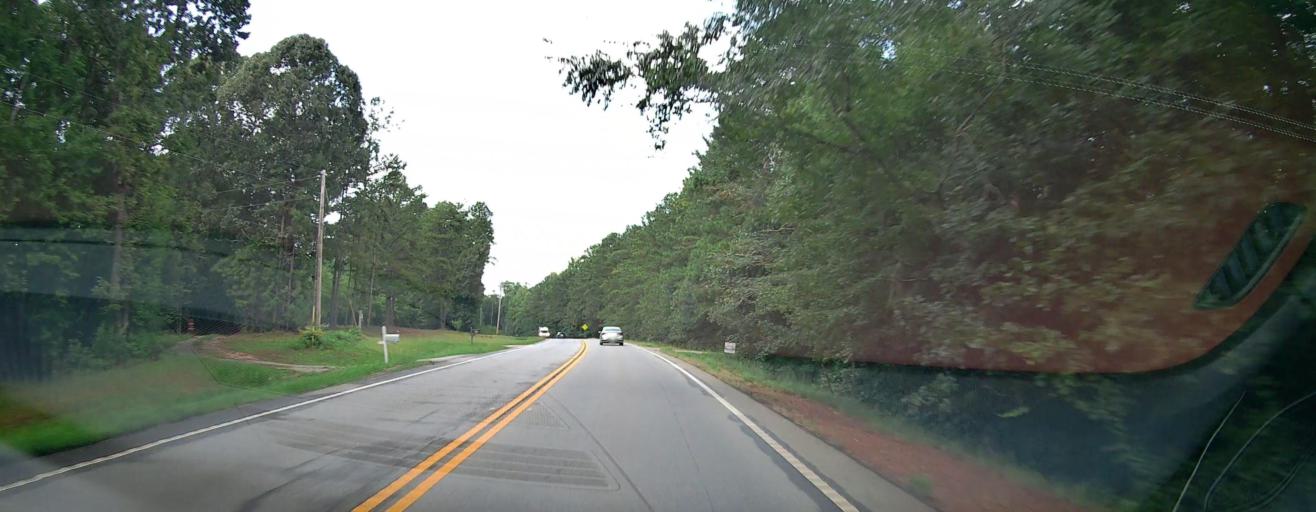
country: US
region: Georgia
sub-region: Coweta County
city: Senoia
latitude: 33.2565
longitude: -84.5555
